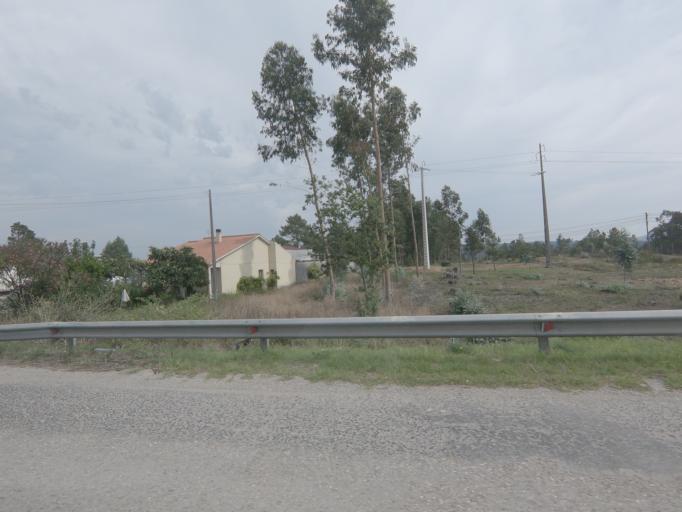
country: PT
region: Leiria
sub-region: Pombal
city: Pombal
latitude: 39.8928
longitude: -8.6592
